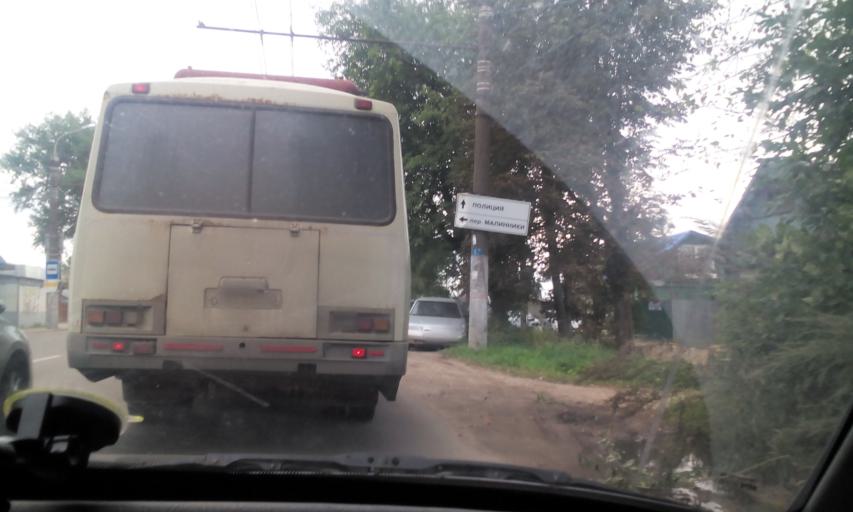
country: RU
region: Kaluga
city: Kaluga
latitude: 54.5548
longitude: 36.2918
